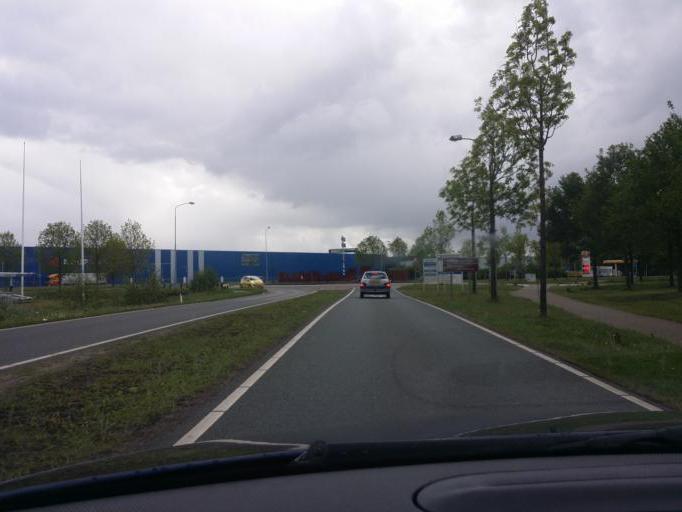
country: NL
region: Groningen
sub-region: Gemeente Hoogezand-Sappemeer
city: Hoogezand
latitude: 53.1688
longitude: 6.7273
